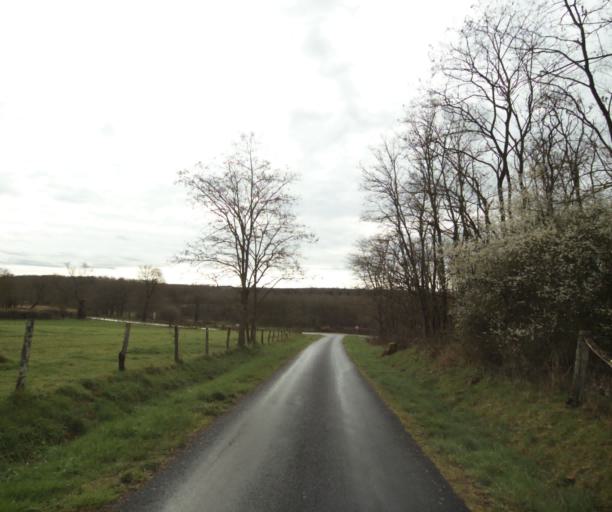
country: FR
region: Auvergne
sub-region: Departement de l'Allier
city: Toulon-sur-Allier
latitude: 46.5166
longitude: 3.3794
